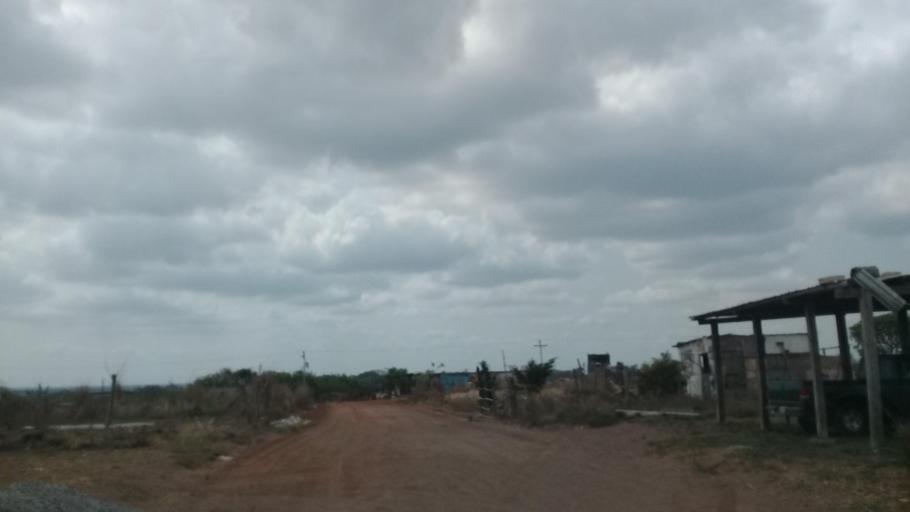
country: MX
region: Veracruz
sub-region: Veracruz
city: Las Amapolas
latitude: 19.1366
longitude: -96.2430
